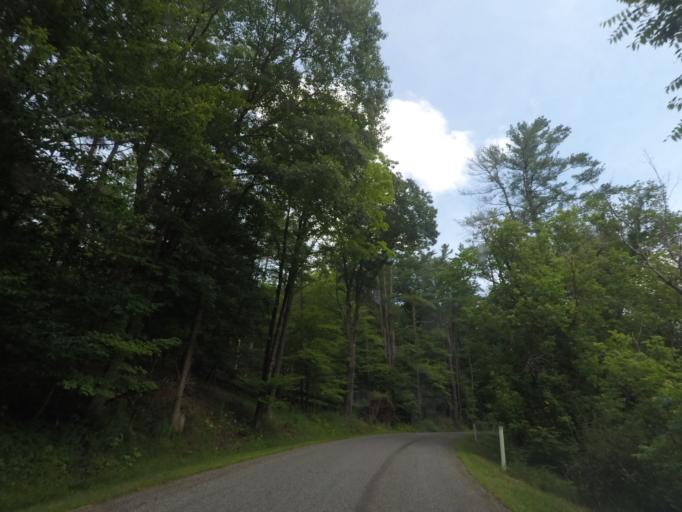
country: US
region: New York
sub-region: Saratoga County
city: Stillwater
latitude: 43.0083
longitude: -73.6199
